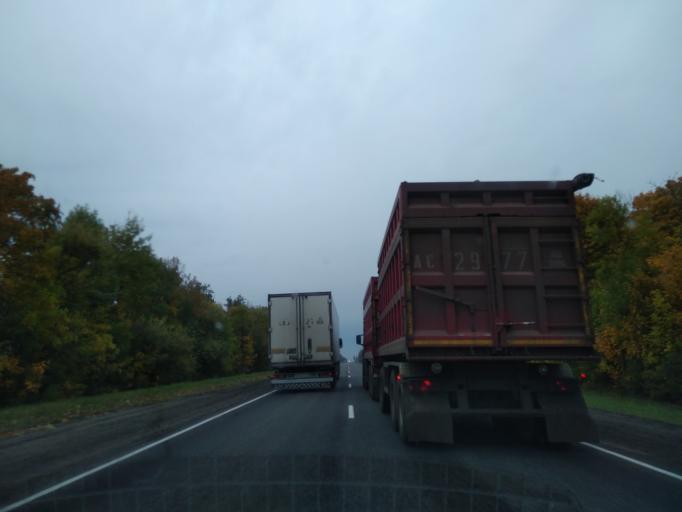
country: RU
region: Lipetsk
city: Zadonsk
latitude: 52.4523
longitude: 38.7802
